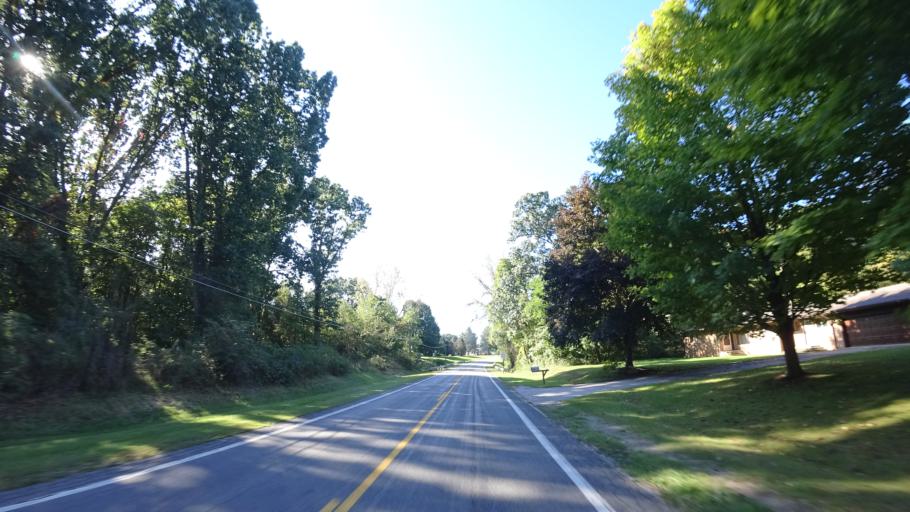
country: US
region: Michigan
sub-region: Berrien County
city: Lake Michigan Beach
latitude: 42.1763
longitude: -86.3854
